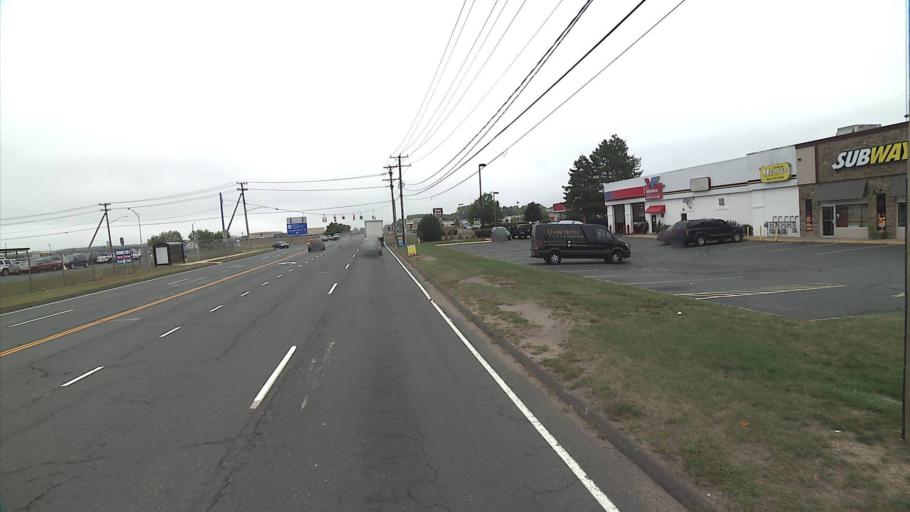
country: US
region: Connecticut
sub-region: Hartford County
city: Windsor Locks
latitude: 41.9239
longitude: -72.6700
